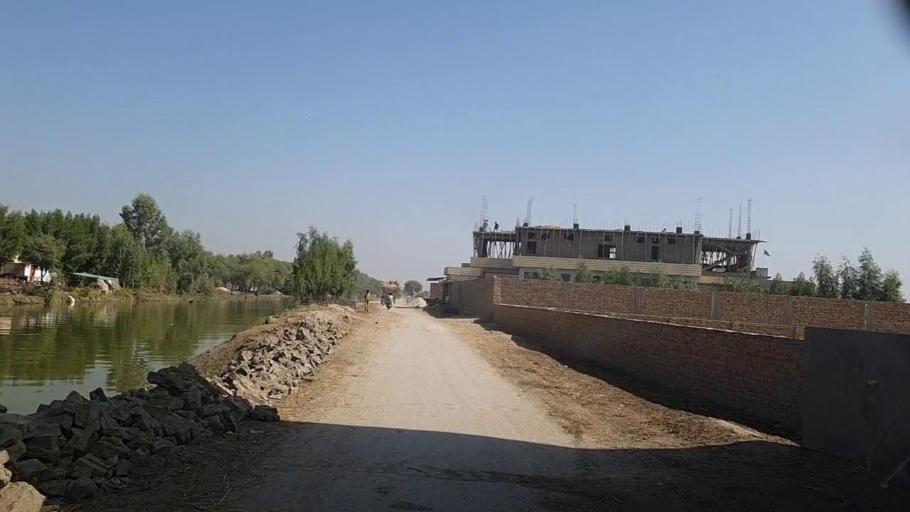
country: PK
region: Sindh
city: Thul
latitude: 28.2370
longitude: 68.7899
